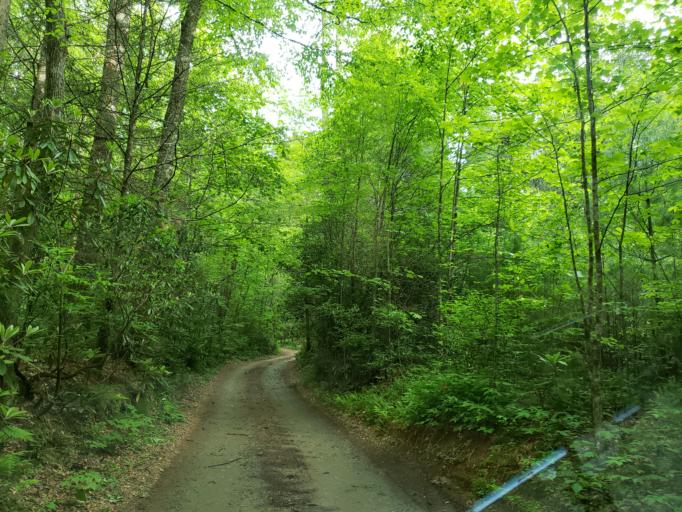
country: US
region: Georgia
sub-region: Fannin County
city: Blue Ridge
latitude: 34.8520
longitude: -84.4415
